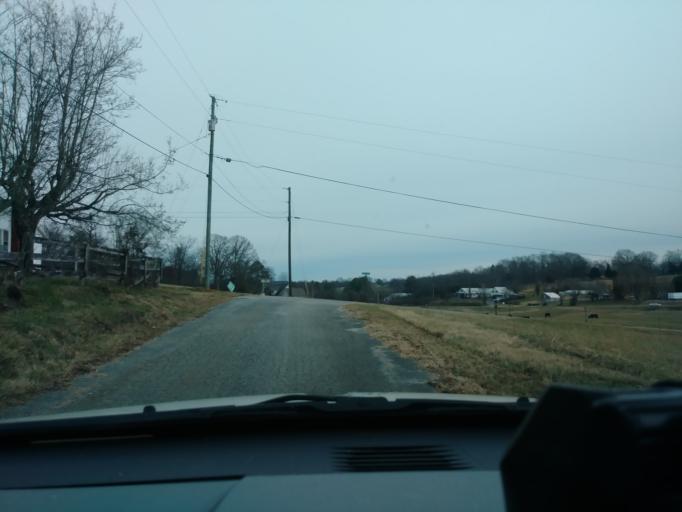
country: US
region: Tennessee
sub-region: Greene County
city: Greeneville
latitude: 36.1181
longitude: -82.8677
